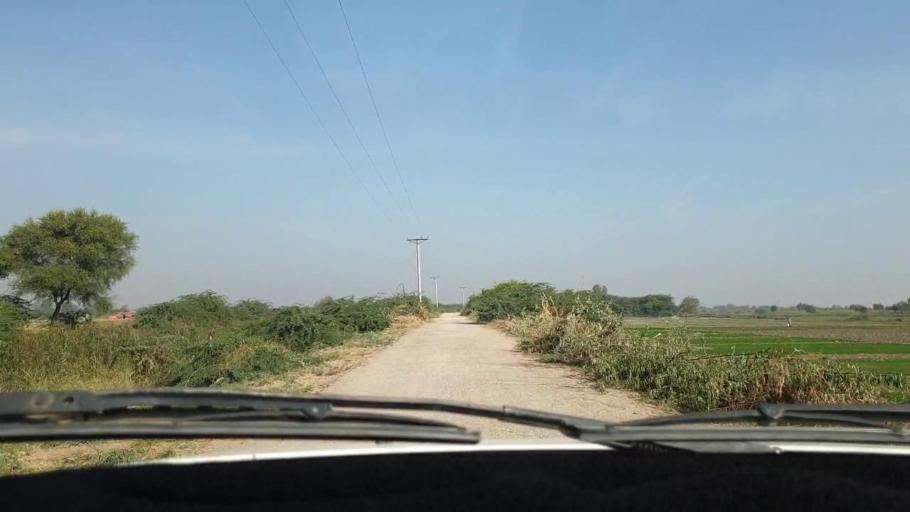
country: PK
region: Sindh
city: Bulri
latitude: 24.9700
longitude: 68.4562
